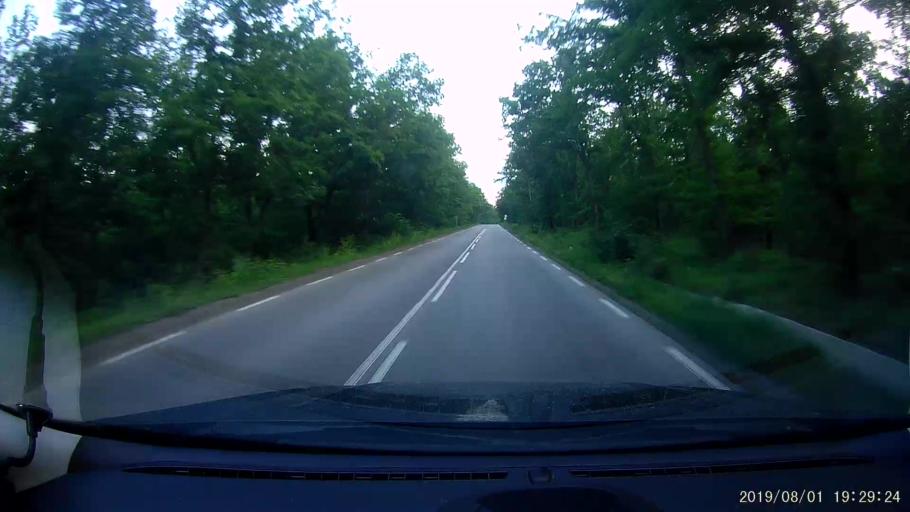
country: BG
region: Burgas
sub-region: Obshtina Sungurlare
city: Sungurlare
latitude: 42.8264
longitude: 26.9078
